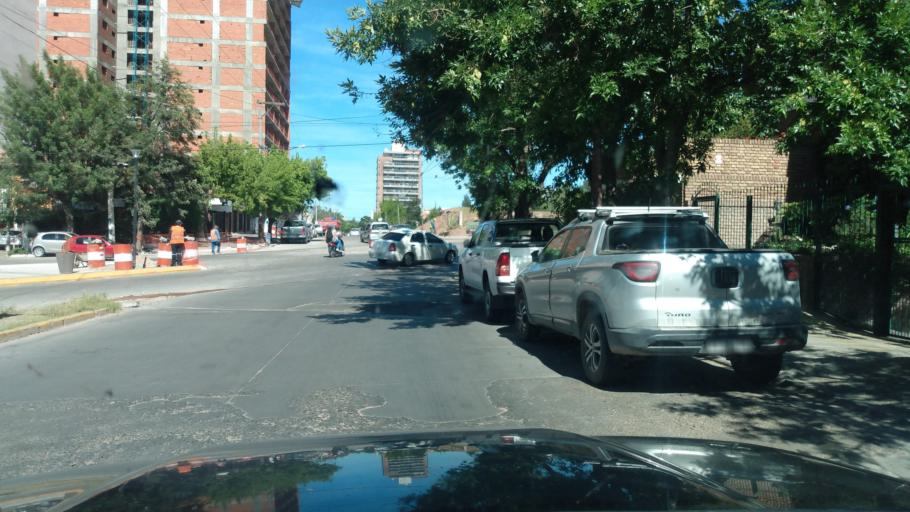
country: AR
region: Neuquen
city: Neuquen
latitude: -38.9475
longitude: -68.0630
